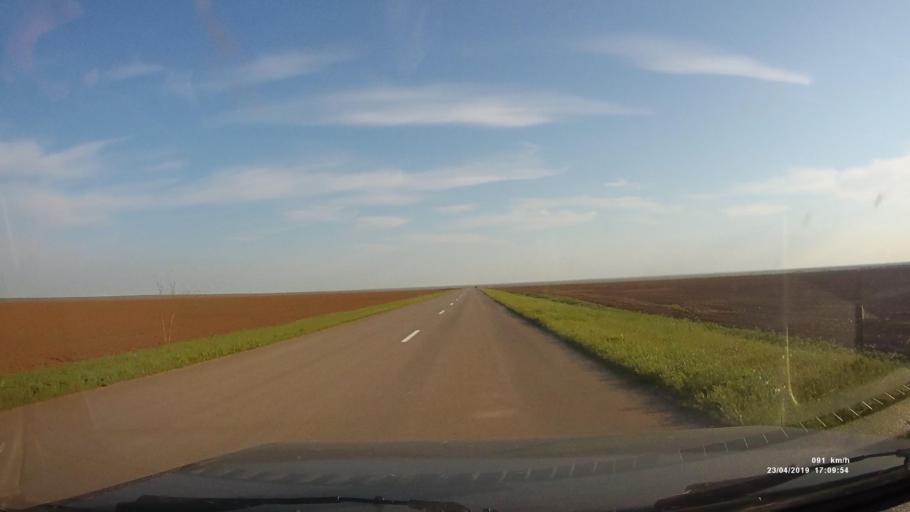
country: RU
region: Kalmykiya
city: Priyutnoye
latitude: 46.2518
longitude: 43.4842
